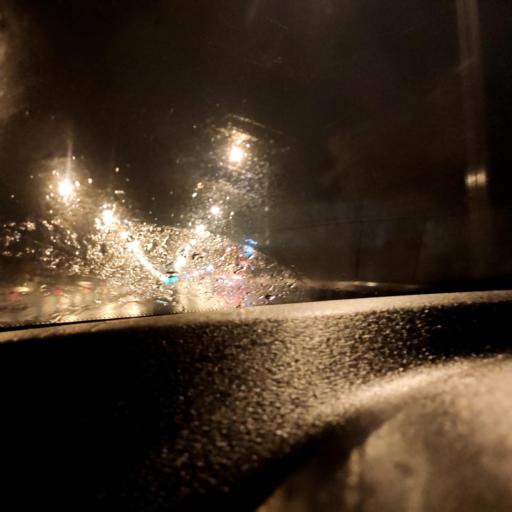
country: RU
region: Samara
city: Petra-Dubrava
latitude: 53.2998
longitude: 50.2428
